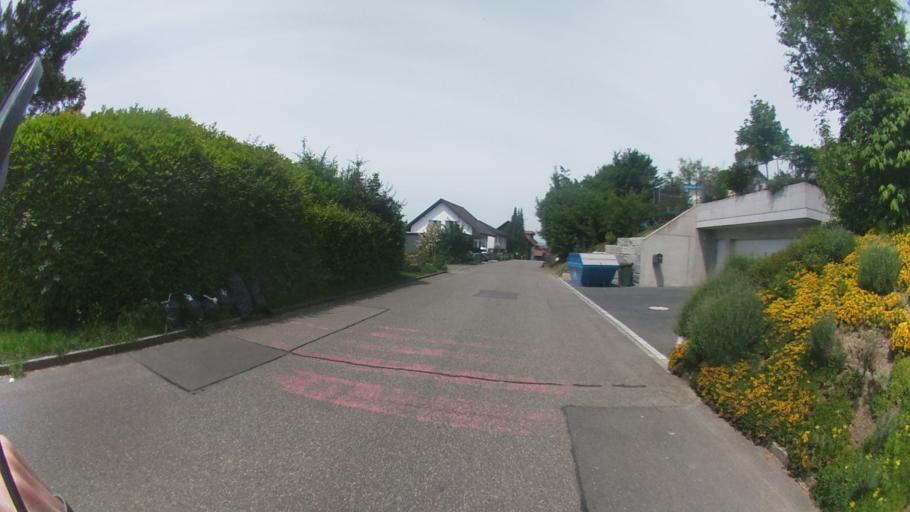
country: CH
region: Aargau
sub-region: Bezirk Zurzach
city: Oberendingen
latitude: 47.5359
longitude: 8.2946
